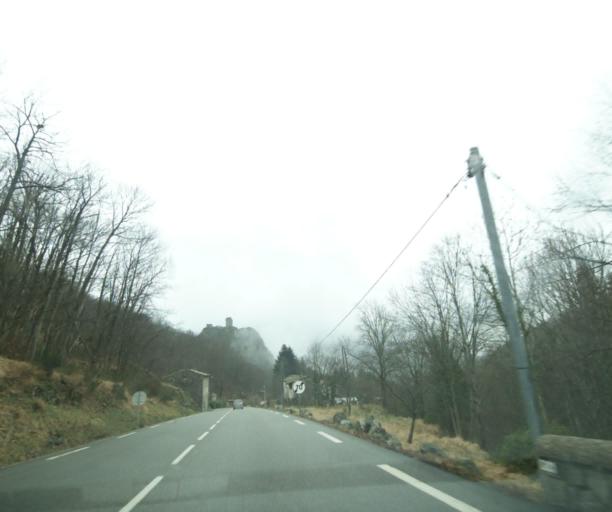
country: FR
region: Rhone-Alpes
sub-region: Departement de l'Ardeche
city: Thueyts
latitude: 44.6765
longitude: 4.0981
